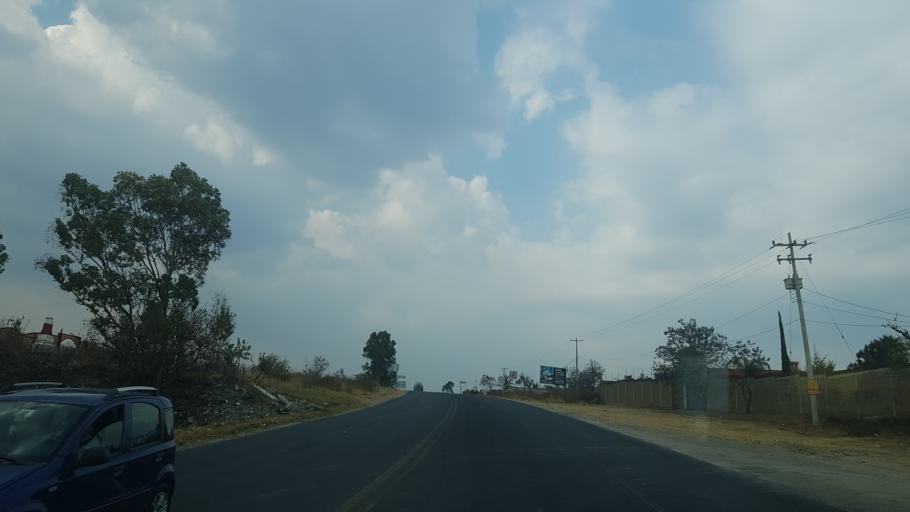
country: MX
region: Puebla
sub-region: Santa Isabel Cholula
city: Santa Ana Acozautla
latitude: 18.9691
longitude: -98.3821
